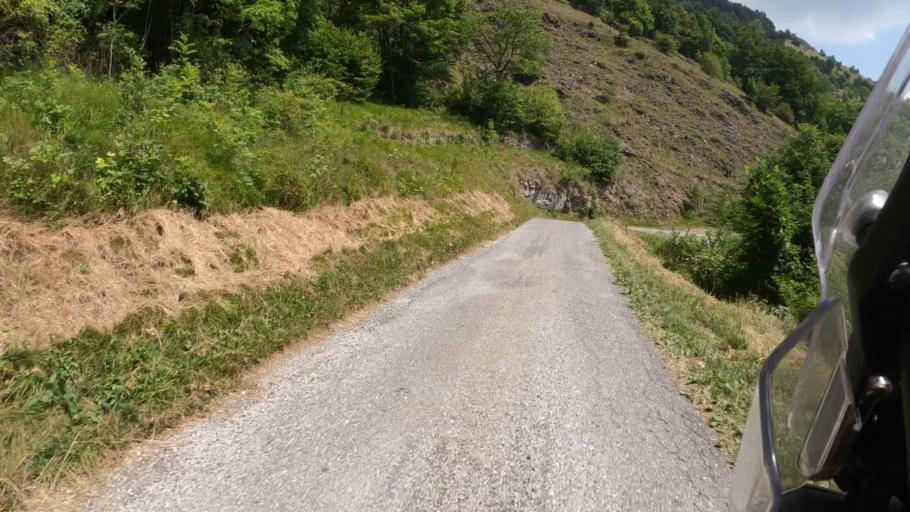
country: IT
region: Piedmont
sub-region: Provincia di Torino
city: Sant'Antonino di Susa
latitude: 45.1495
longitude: 7.2767
